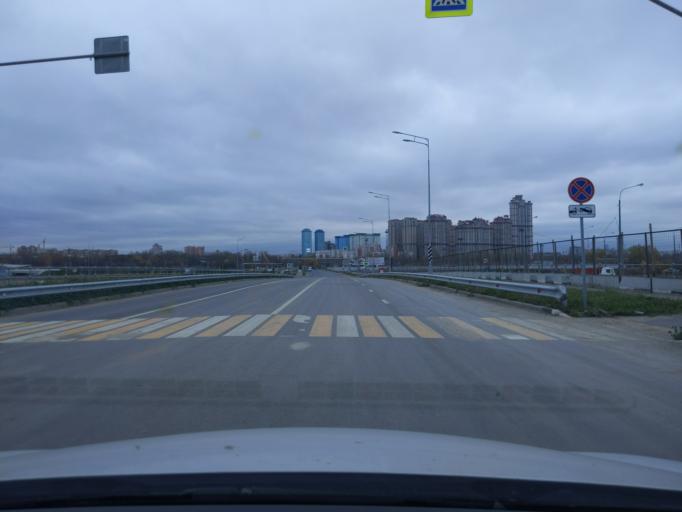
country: RU
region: Moscow
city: Strogino
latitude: 55.8152
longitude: 37.4314
